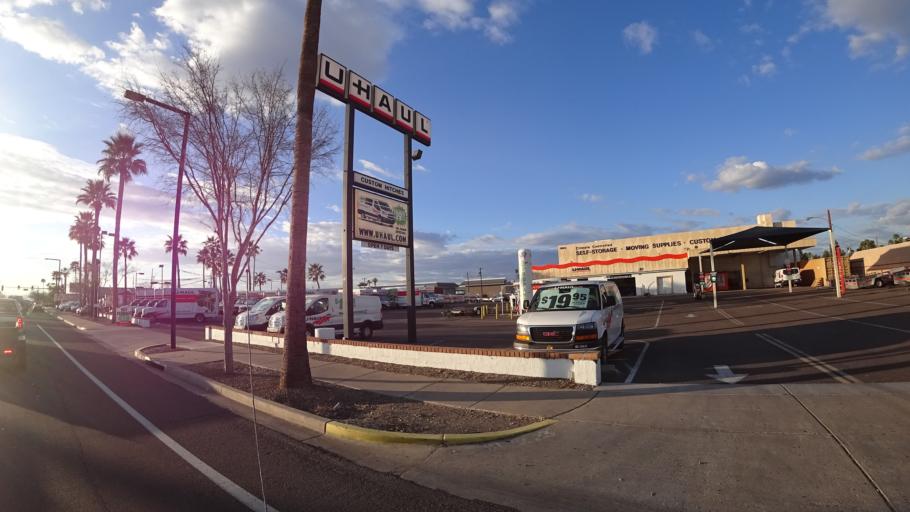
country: US
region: Arizona
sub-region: Maricopa County
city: Glendale
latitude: 33.5385
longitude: -112.1671
